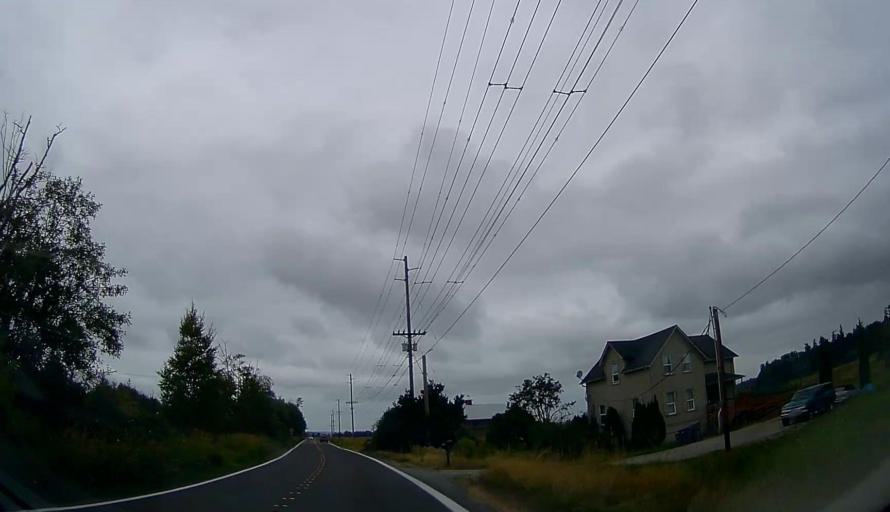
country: US
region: Washington
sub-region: Snohomish County
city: Stanwood
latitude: 48.2283
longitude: -122.3409
